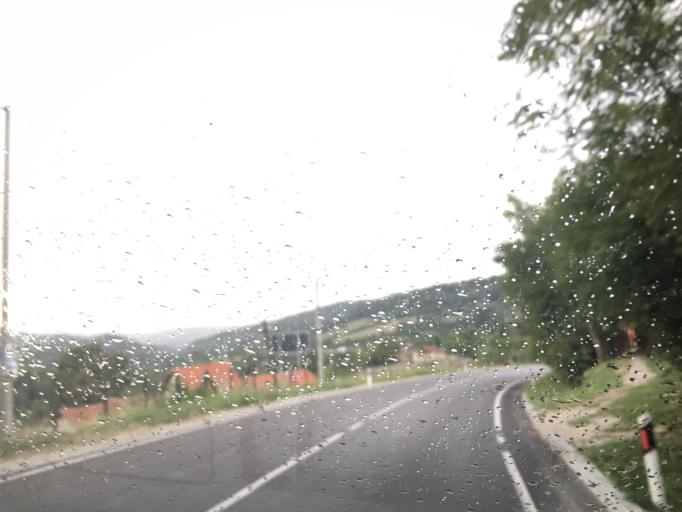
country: RS
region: Central Serbia
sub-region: Moravicki Okrug
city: Gornji Milanovac
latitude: 44.1229
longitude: 20.4859
